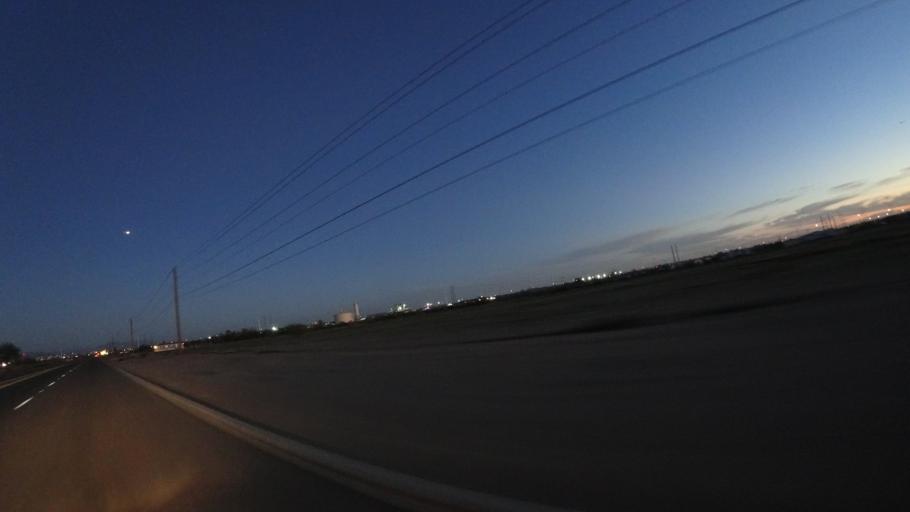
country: US
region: Arizona
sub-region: Maricopa County
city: Tempe
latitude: 33.4512
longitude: -111.8815
